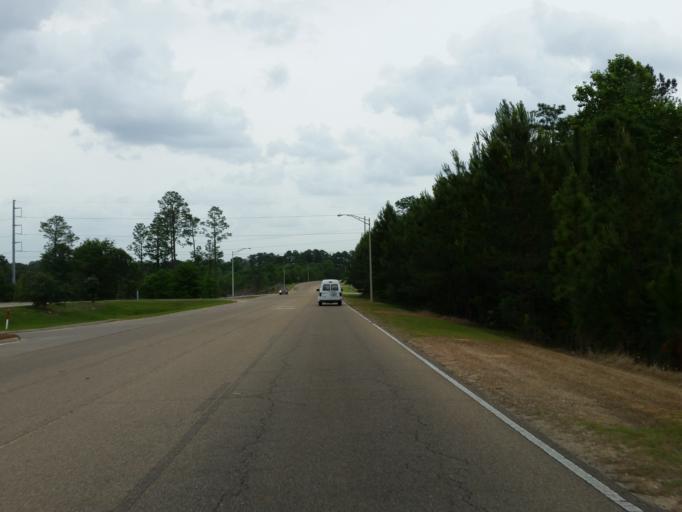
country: US
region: Mississippi
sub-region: Lamar County
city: West Hattiesburg
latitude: 31.3033
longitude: -89.3580
